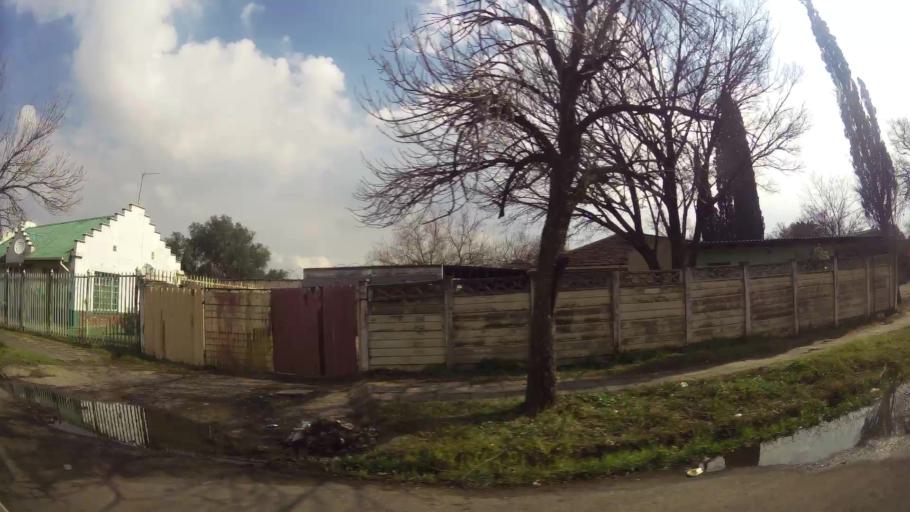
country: ZA
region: Gauteng
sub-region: Sedibeng District Municipality
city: Vereeniging
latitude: -26.6760
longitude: 27.9202
